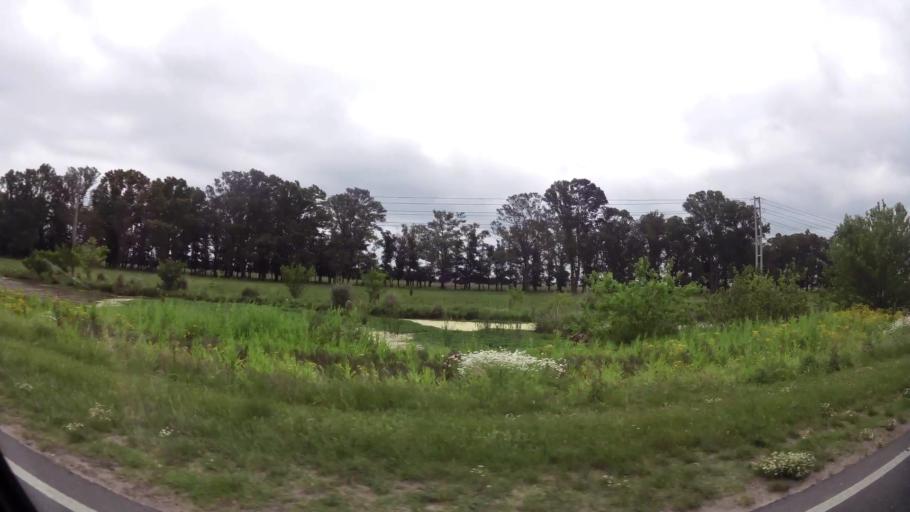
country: AR
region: Buenos Aires
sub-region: Partido de San Vicente
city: San Vicente
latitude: -34.9810
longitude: -58.4680
